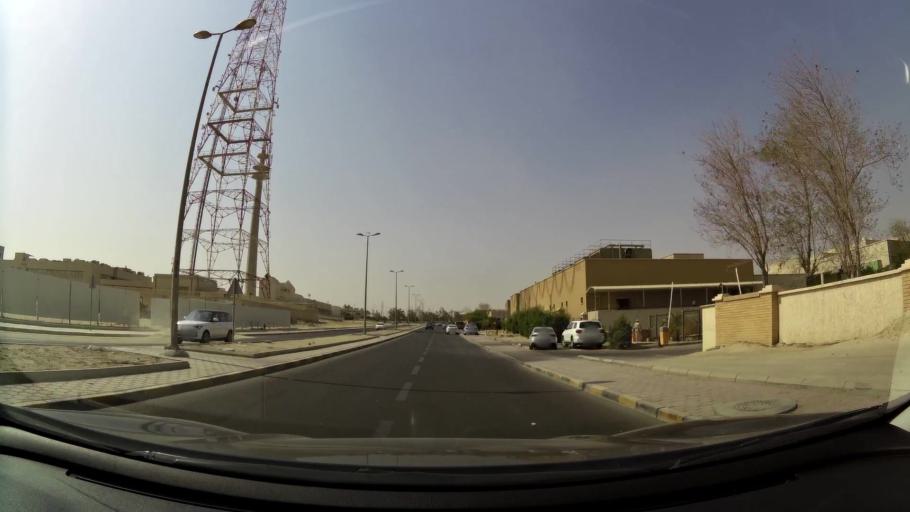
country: KW
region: Al Ahmadi
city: Al Fahahil
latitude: 29.0882
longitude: 48.1084
